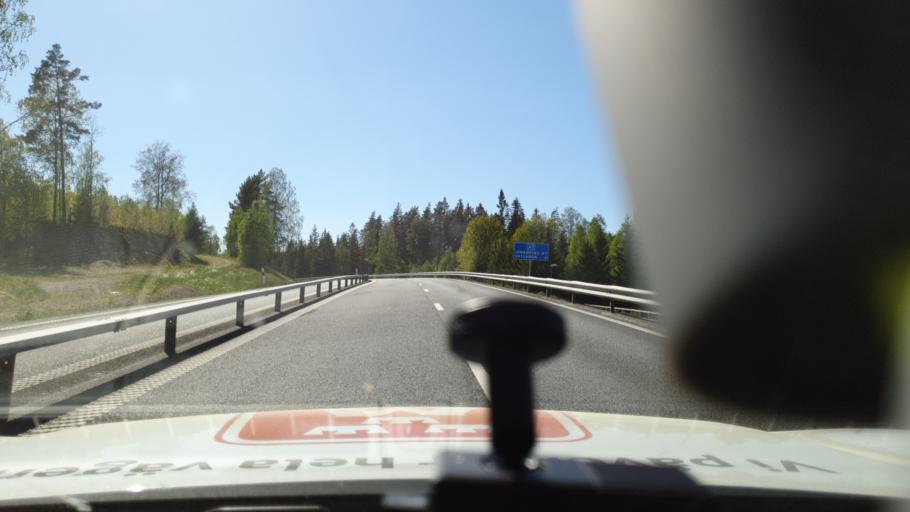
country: SE
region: Joenkoeping
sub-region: Vetlanda Kommun
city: Vetlanda
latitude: 57.4315
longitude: 15.1673
